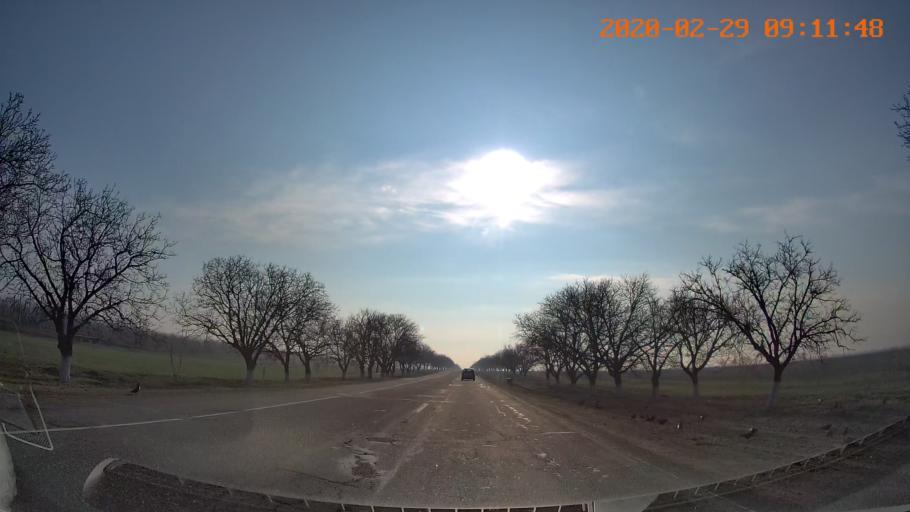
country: MD
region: Telenesti
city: Slobozia
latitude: 46.8319
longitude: 29.8063
